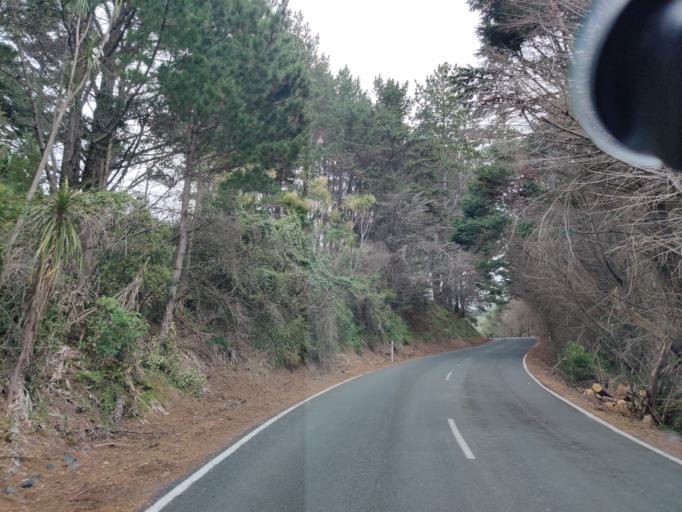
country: NZ
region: Auckland
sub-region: Auckland
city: Warkworth
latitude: -36.2821
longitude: 174.7885
